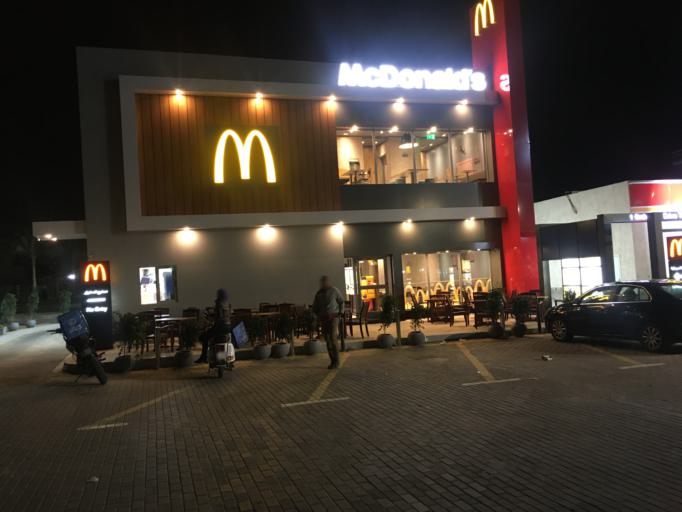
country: EG
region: Al Jizah
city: Awsim
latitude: 30.0155
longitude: 30.9753
